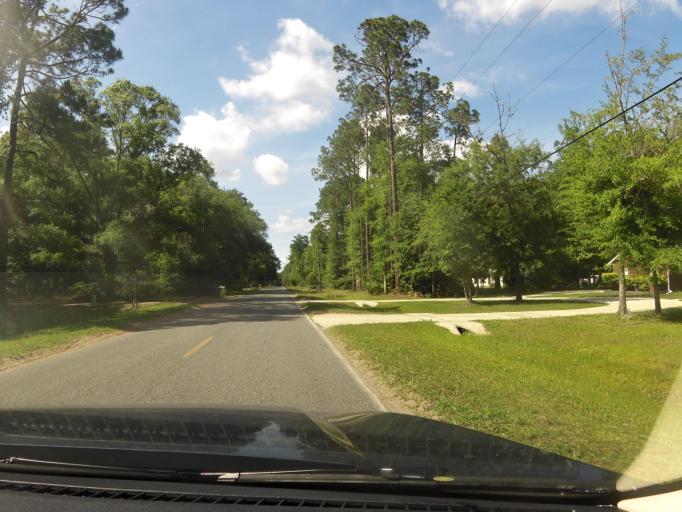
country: US
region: Florida
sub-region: Nassau County
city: Hilliard
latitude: 30.6767
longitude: -81.9216
